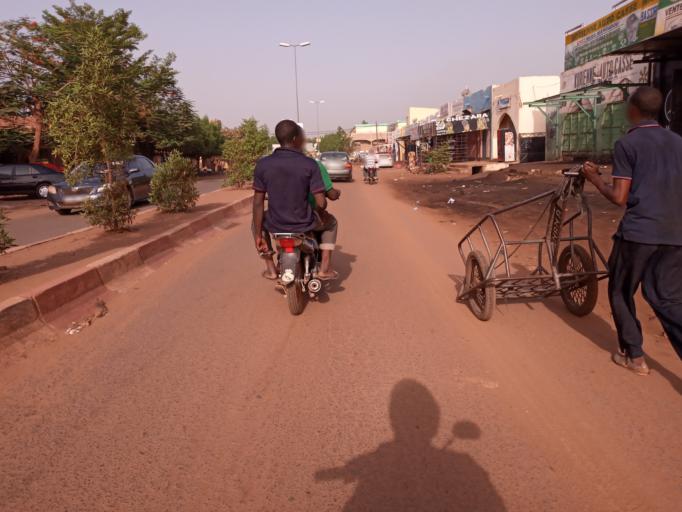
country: ML
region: Bamako
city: Bamako
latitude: 12.6612
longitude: -7.9795
